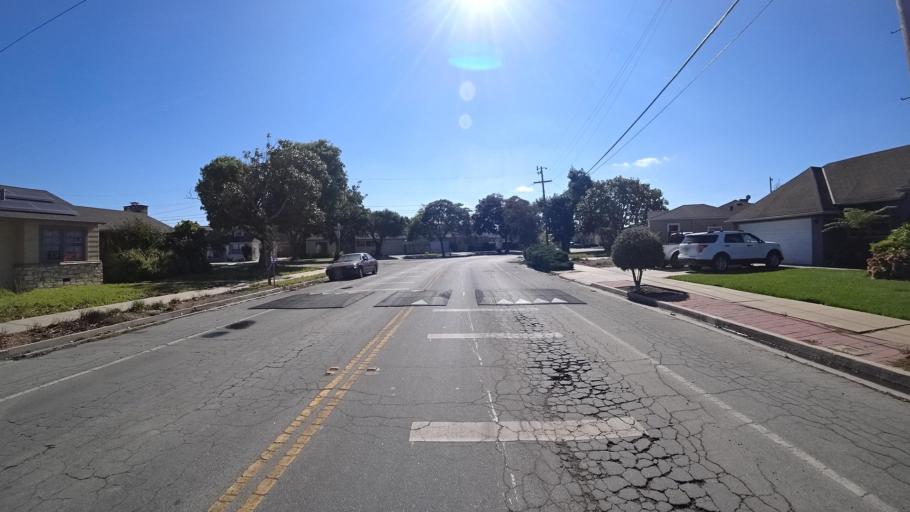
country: US
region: California
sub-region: Monterey County
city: Salinas
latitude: 36.6774
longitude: -121.6703
